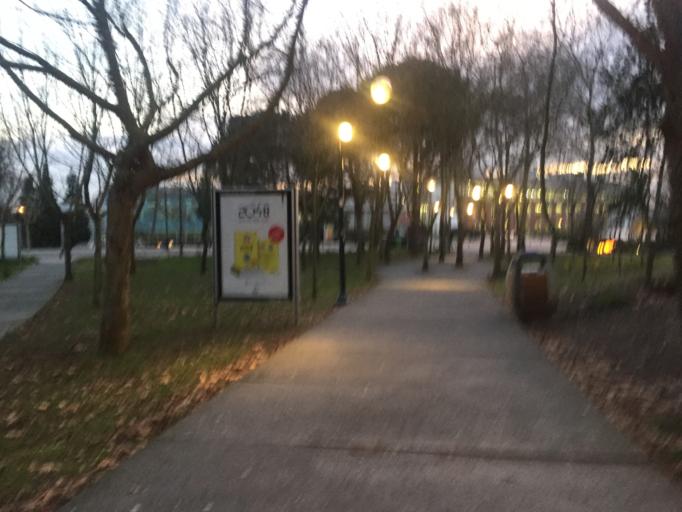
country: TR
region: Istanbul
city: Sisli
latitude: 41.1051
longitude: 29.0220
